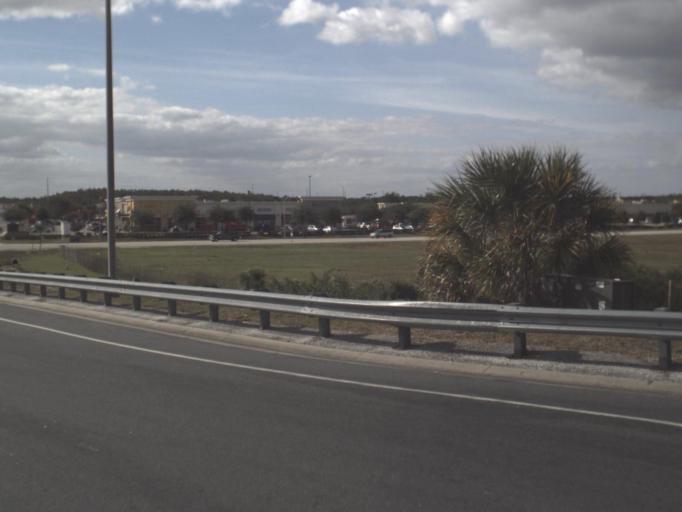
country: US
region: Florida
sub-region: Osceola County
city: Buenaventura Lakes
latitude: 28.3408
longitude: -81.3815
